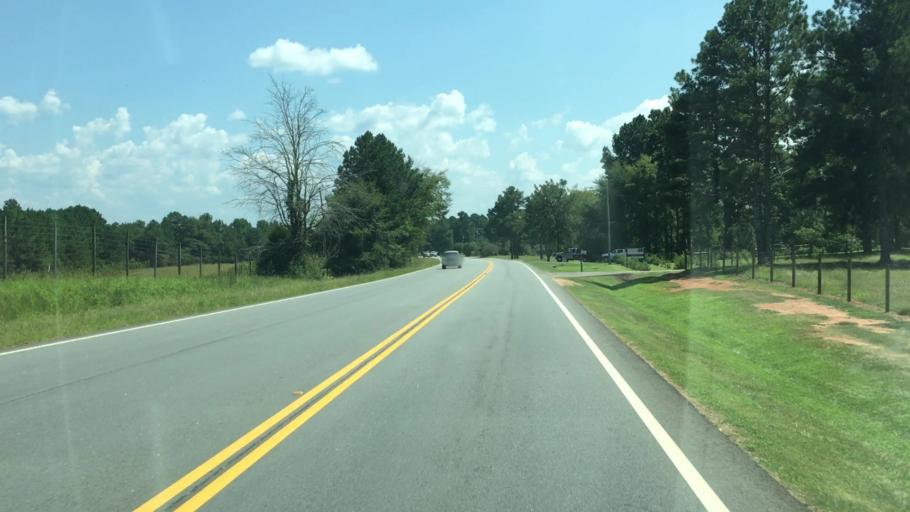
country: US
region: Georgia
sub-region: Oconee County
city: Watkinsville
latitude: 33.7448
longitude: -83.4323
